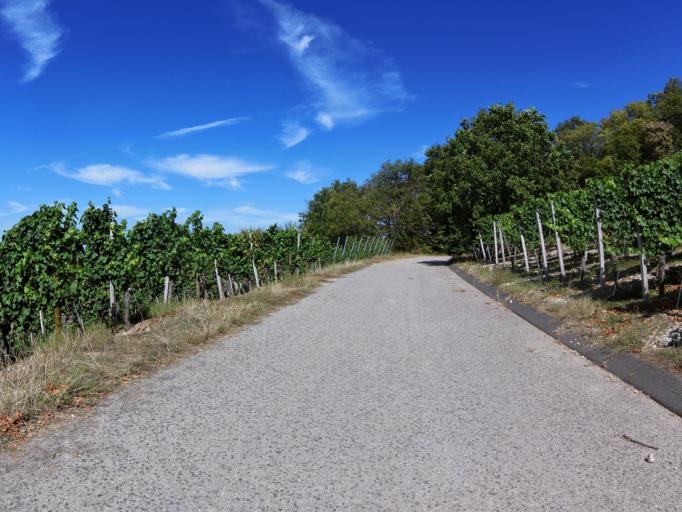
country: DE
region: Bavaria
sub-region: Regierungsbezirk Unterfranken
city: Thungersheim
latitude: 49.8720
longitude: 9.8573
